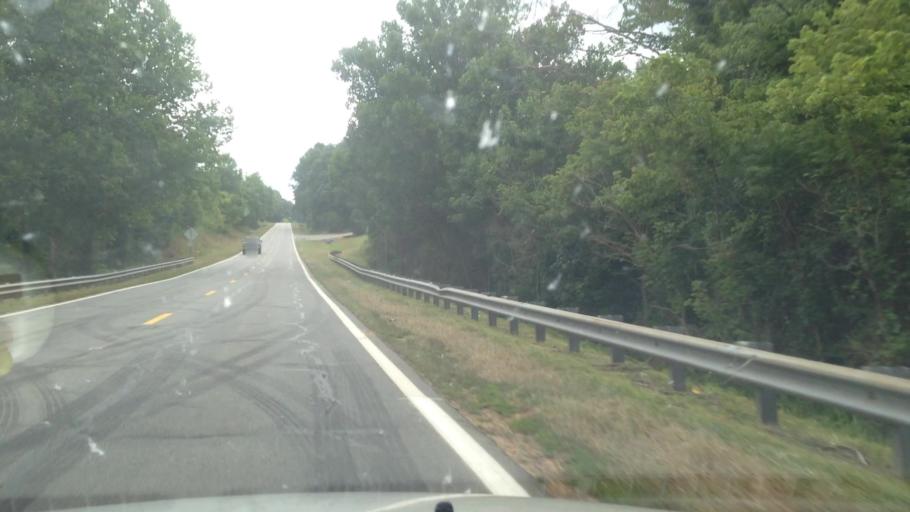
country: US
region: North Carolina
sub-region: Rockingham County
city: Madison
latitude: 36.3796
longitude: -79.8755
